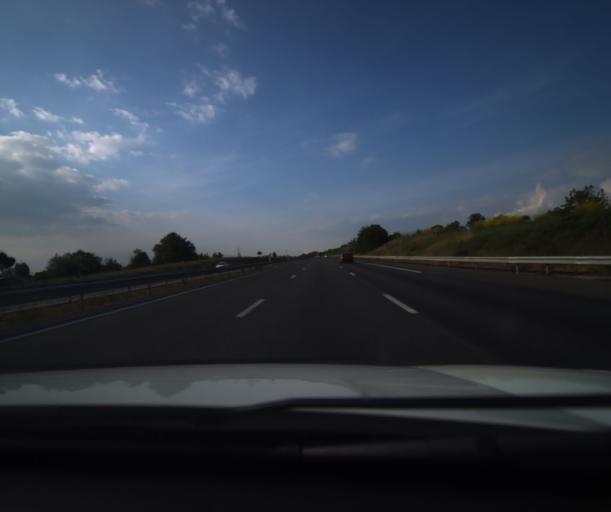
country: FR
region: Midi-Pyrenees
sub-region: Departement de la Haute-Garonne
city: Bouloc
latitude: 43.7803
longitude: 1.3833
